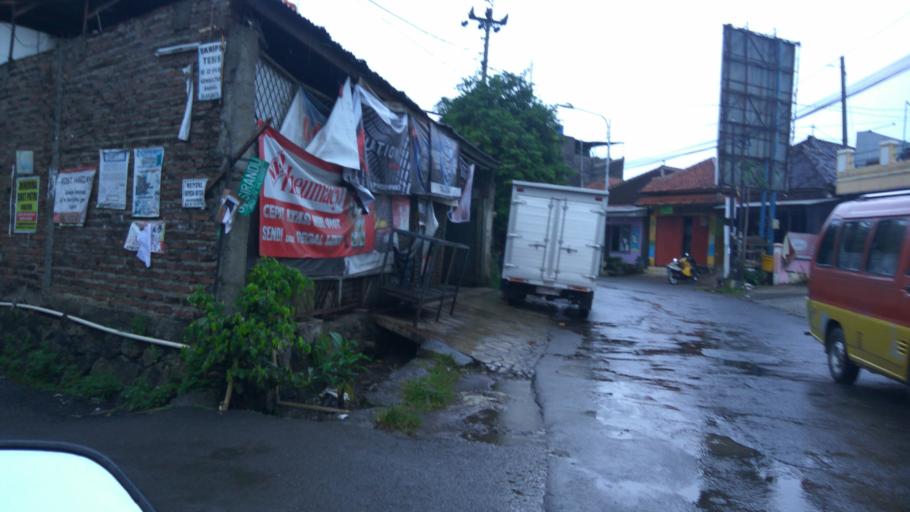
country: ID
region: Central Java
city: Semarang
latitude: -7.0465
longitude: 110.3946
